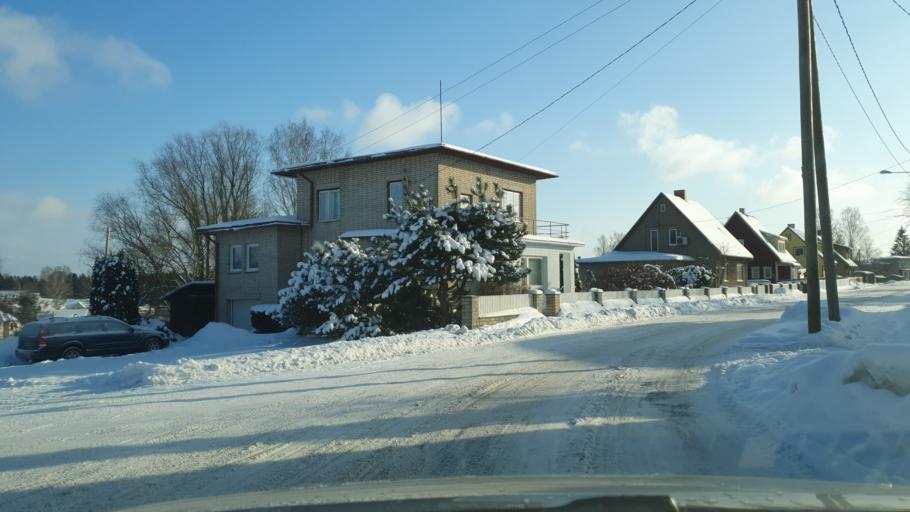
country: EE
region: Viljandimaa
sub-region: Viiratsi vald
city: Viiratsi
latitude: 58.3694
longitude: 25.6149
